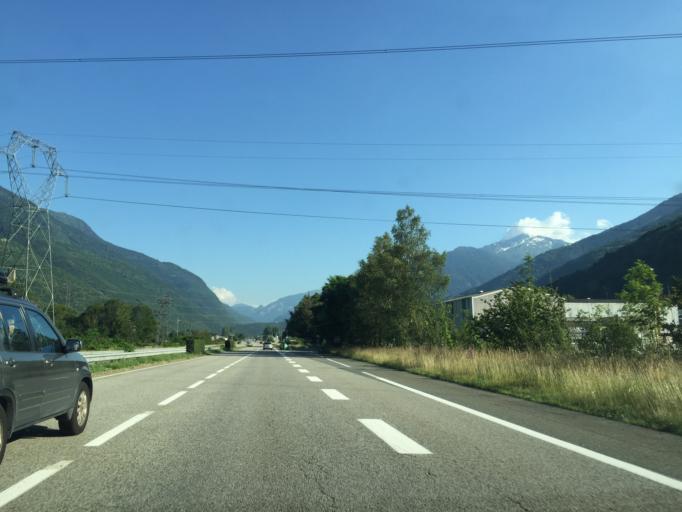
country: FR
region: Rhone-Alpes
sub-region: Departement de la Savoie
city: La Bathie
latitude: 45.6459
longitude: 6.4382
